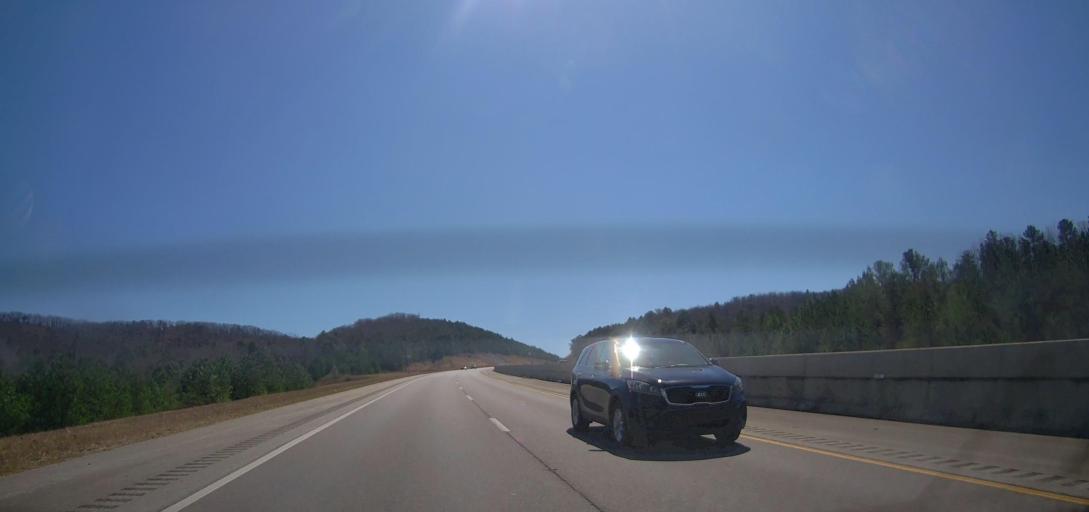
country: US
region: Alabama
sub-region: Calhoun County
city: Anniston
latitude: 33.6726
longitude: -85.7905
